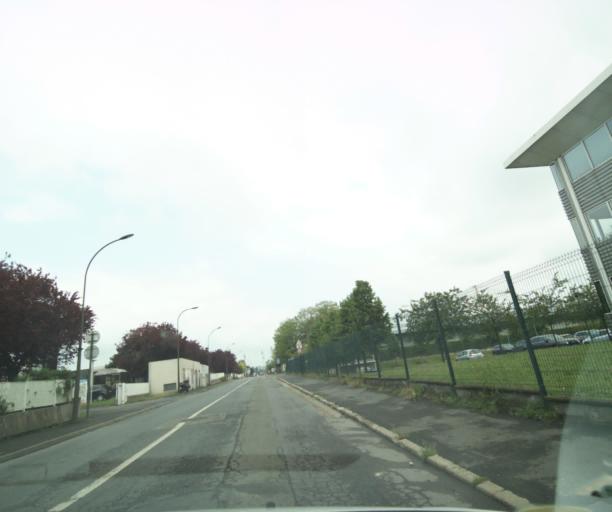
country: FR
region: Ile-de-France
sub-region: Departement des Hauts-de-Seine
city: Colombes
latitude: 48.9311
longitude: 2.2351
